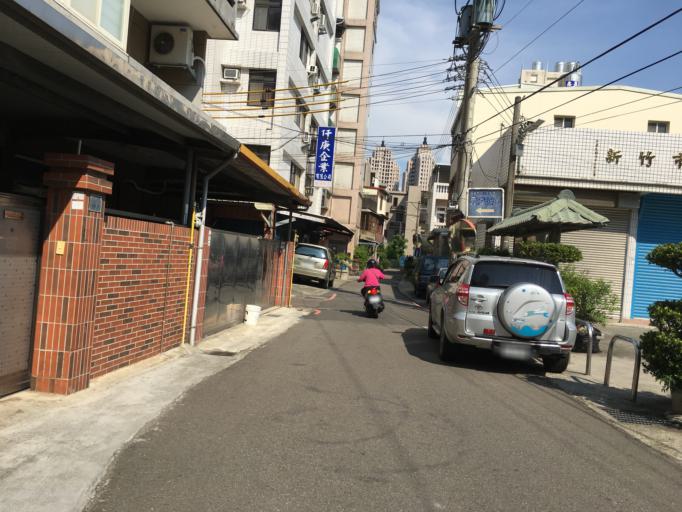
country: TW
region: Taiwan
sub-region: Hsinchu
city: Hsinchu
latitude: 24.7908
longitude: 121.0074
